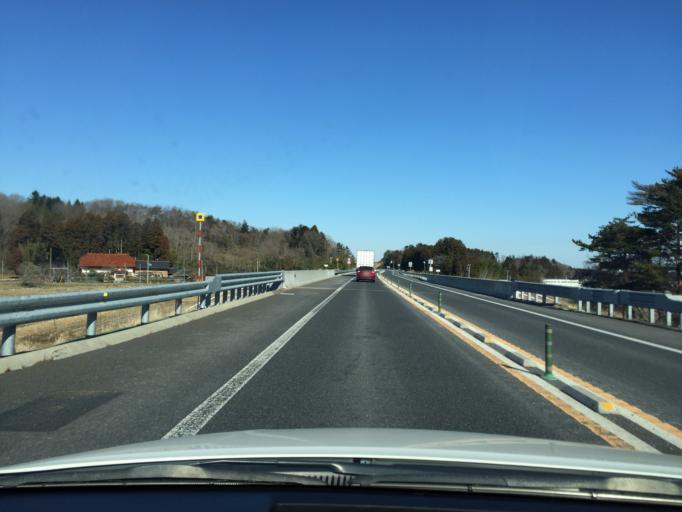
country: JP
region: Miyagi
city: Marumori
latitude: 37.7581
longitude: 140.9018
